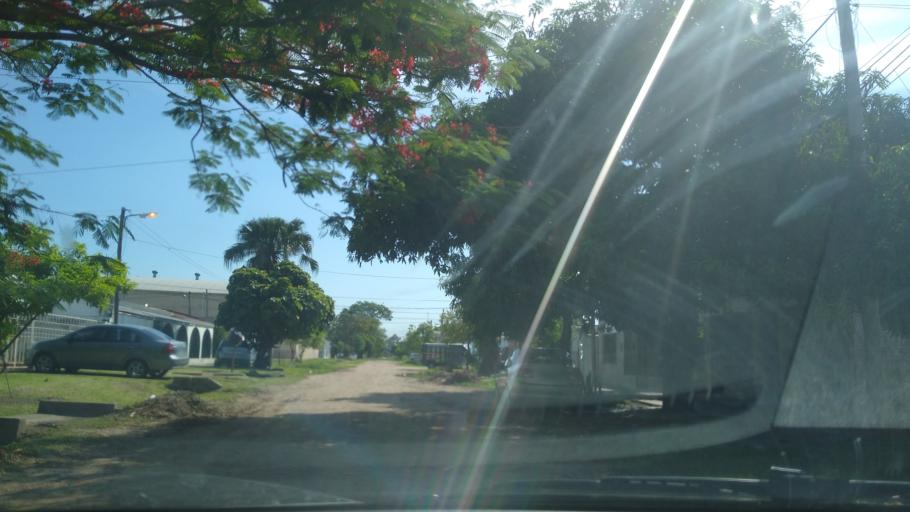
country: AR
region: Chaco
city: Barranqueras
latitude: -27.4866
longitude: -58.9525
